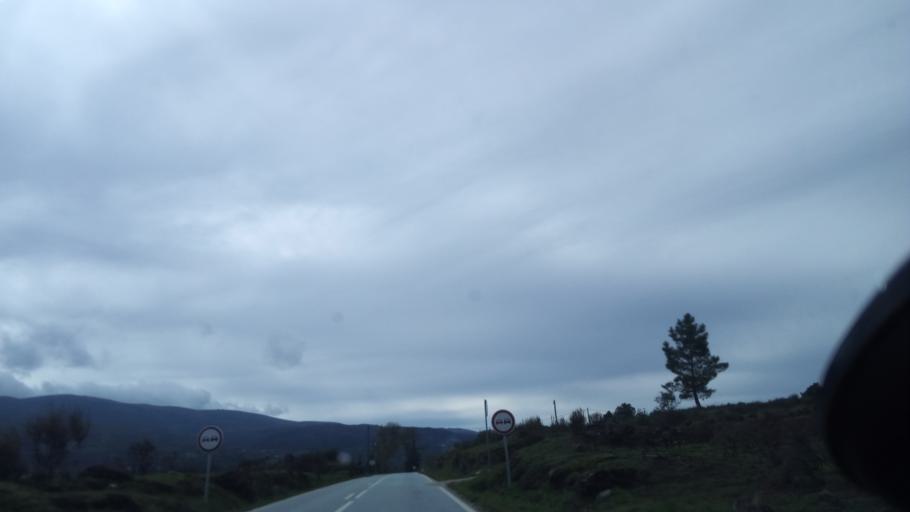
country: PT
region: Guarda
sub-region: Fornos de Algodres
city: Fornos de Algodres
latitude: 40.5465
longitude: -7.5687
